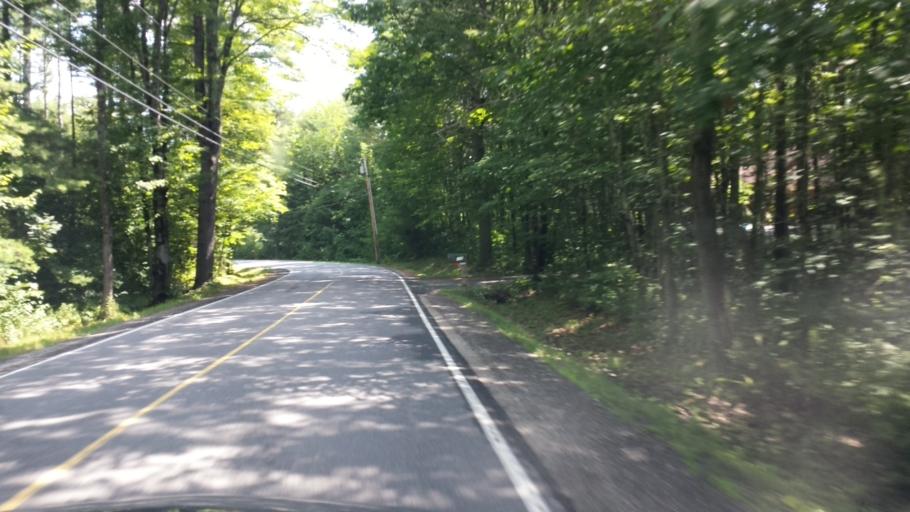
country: US
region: Maine
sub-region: York County
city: Kennebunk
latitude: 43.4468
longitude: -70.5199
